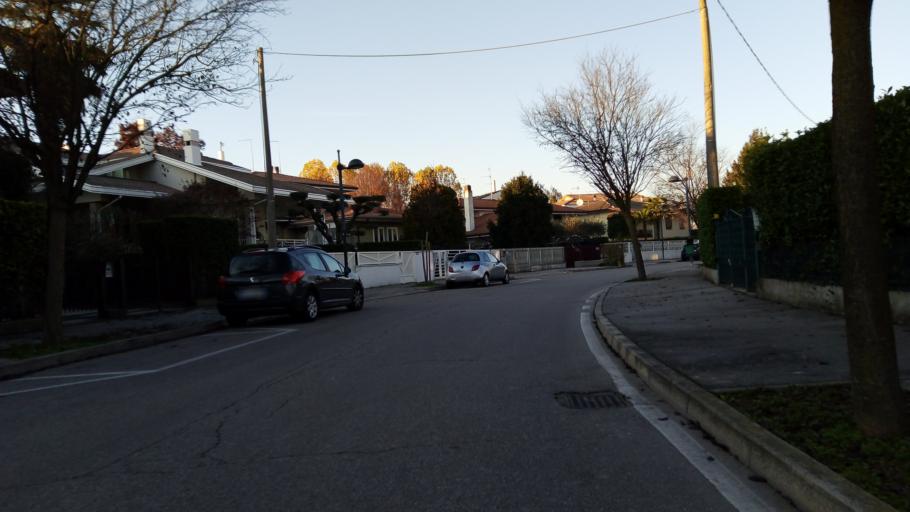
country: IT
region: Veneto
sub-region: Provincia di Padova
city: Abano Terme
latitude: 45.3672
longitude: 11.7917
